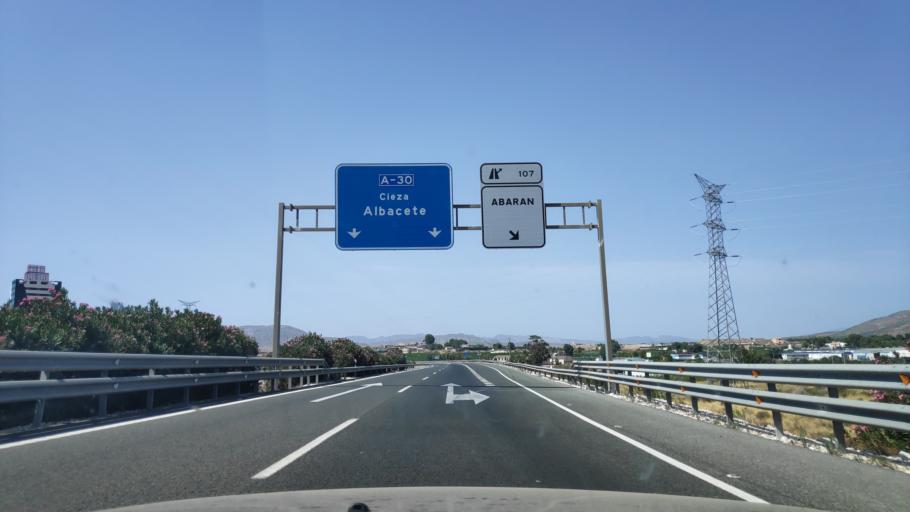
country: ES
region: Murcia
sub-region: Murcia
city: Blanca
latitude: 38.2124
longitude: -1.3515
